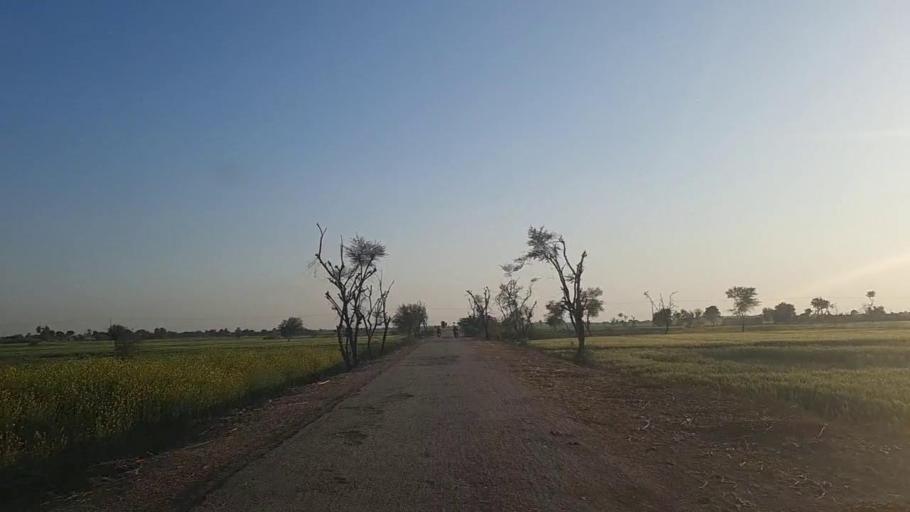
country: PK
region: Sindh
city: Jam Sahib
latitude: 26.3402
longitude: 68.6958
